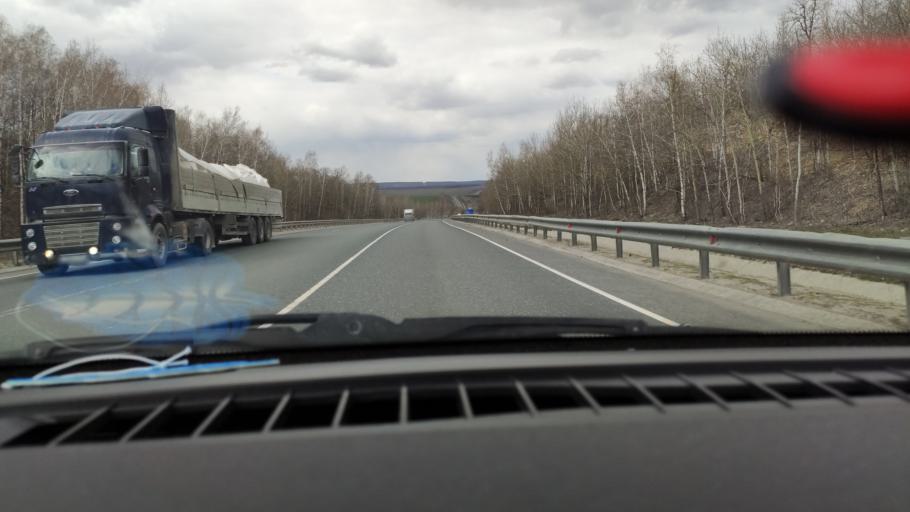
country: RU
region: Saratov
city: Vol'sk
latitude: 52.1134
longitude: 47.3142
